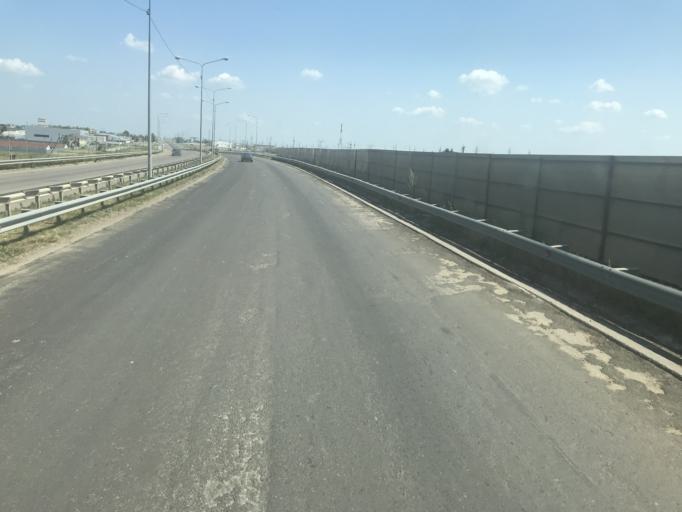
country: KZ
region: Aqmola
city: Kokshetau
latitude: 53.3169
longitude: 69.4034
